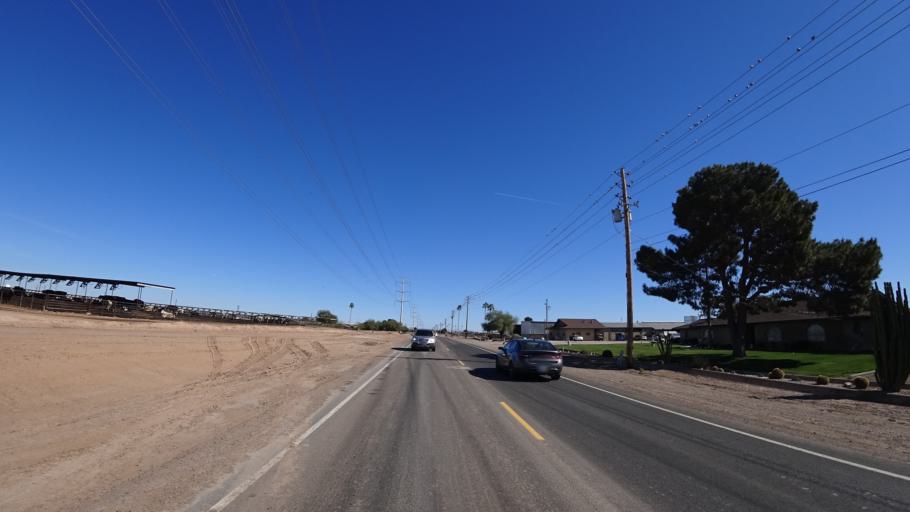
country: US
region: Arizona
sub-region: Maricopa County
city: Tolleson
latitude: 33.4068
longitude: -112.2526
